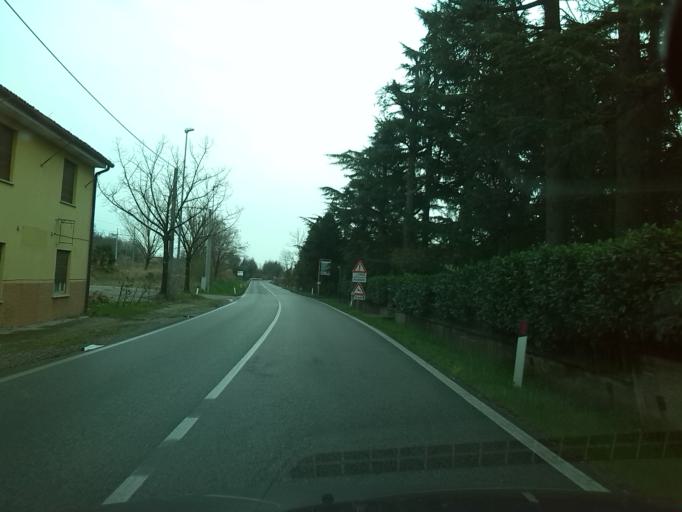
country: IT
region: Friuli Venezia Giulia
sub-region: Provincia di Gorizia
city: Moraro
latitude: 45.9462
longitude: 13.4849
